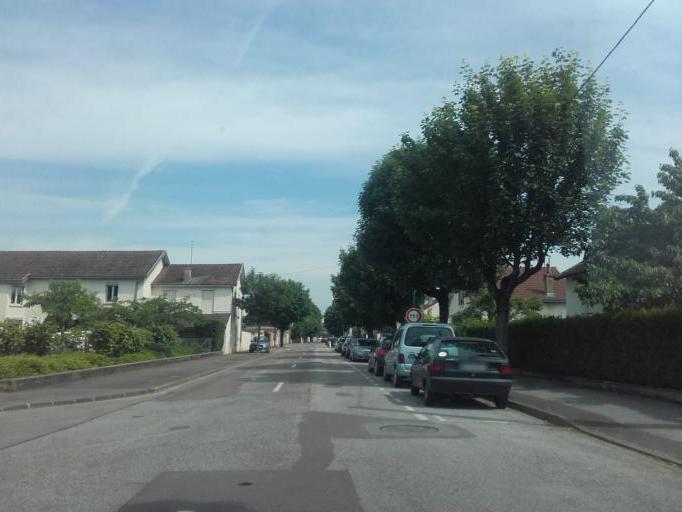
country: FR
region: Bourgogne
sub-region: Departement de la Cote-d'Or
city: Beaune
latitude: 47.0282
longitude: 4.8460
